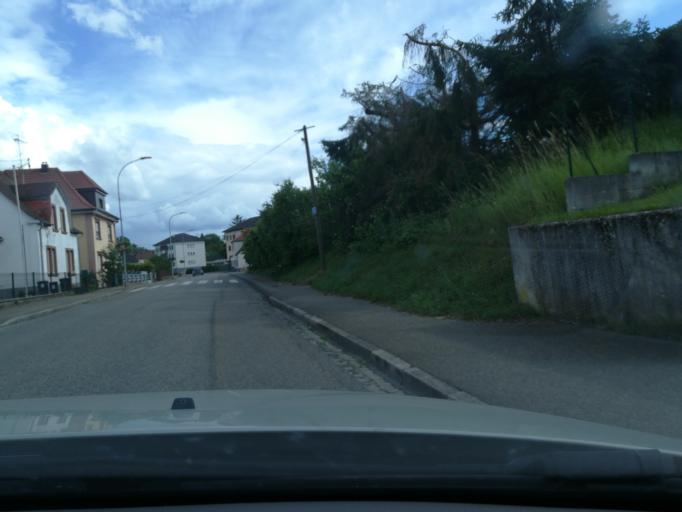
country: FR
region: Alsace
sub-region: Departement du Bas-Rhin
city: Ingwiller
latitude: 48.8670
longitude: 7.4804
